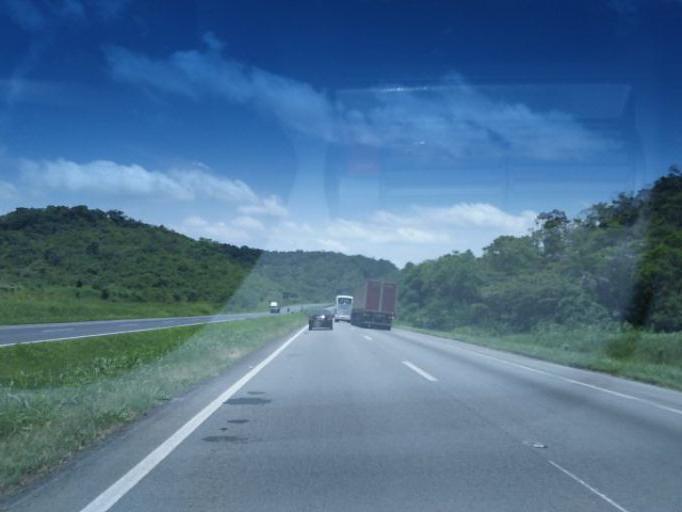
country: BR
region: Sao Paulo
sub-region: Juquia
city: Juquia
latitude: -24.3959
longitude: -47.7277
